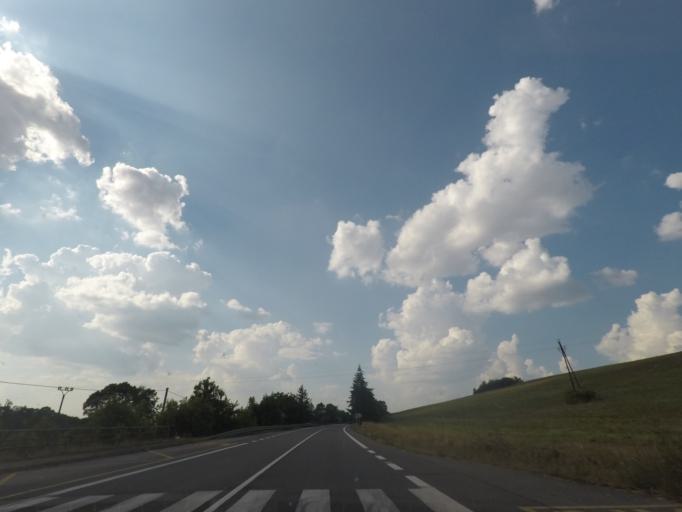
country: CZ
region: Kralovehradecky
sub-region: Okres Nachod
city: Jaromer
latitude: 50.3966
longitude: 15.8993
